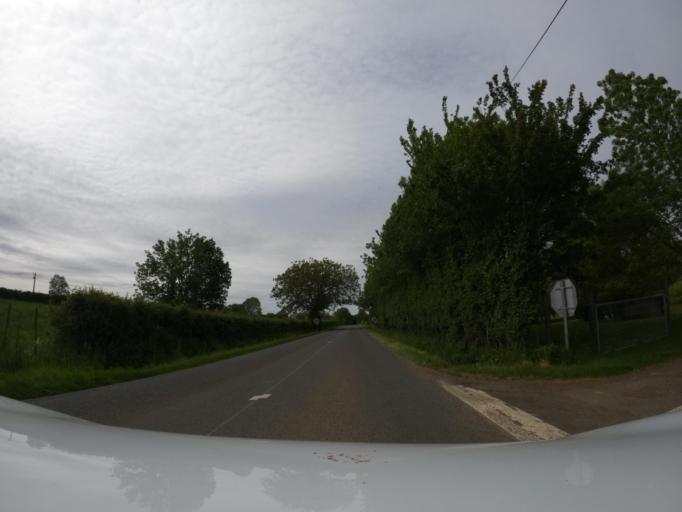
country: FR
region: Pays de la Loire
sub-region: Departement de la Vendee
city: Saint-Hilaire-des-Loges
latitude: 46.4962
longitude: -0.6672
